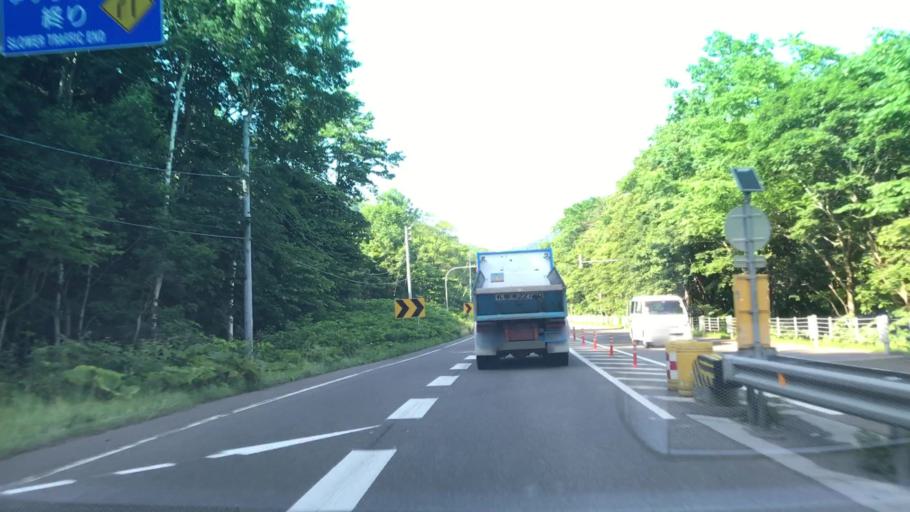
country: JP
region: Hokkaido
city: Iwanai
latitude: 43.0183
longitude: 140.6668
